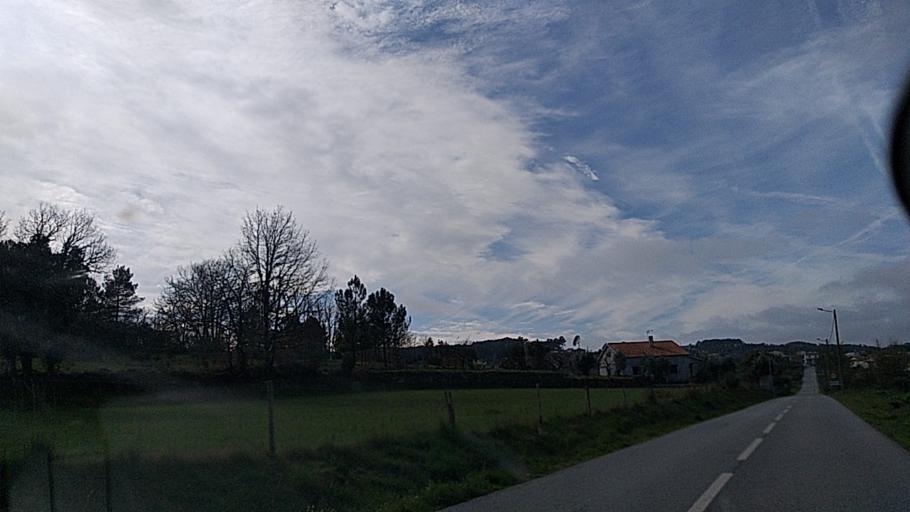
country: PT
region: Guarda
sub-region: Fornos de Algodres
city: Fornos de Algodres
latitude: 40.6623
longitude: -7.5309
